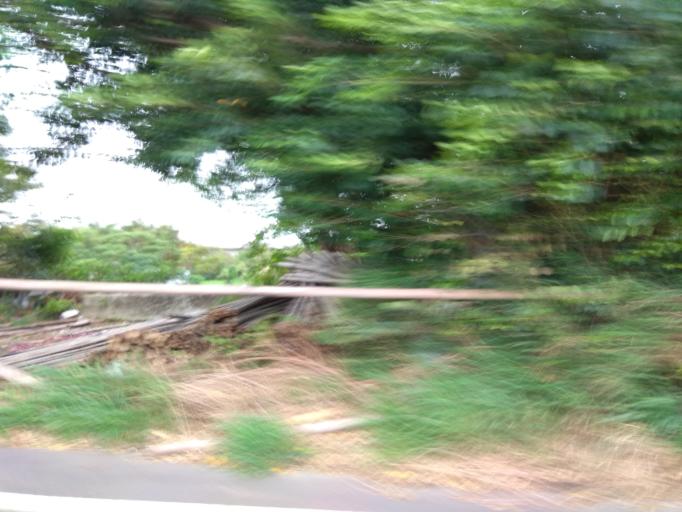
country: TW
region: Taiwan
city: Taoyuan City
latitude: 25.0510
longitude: 121.2141
